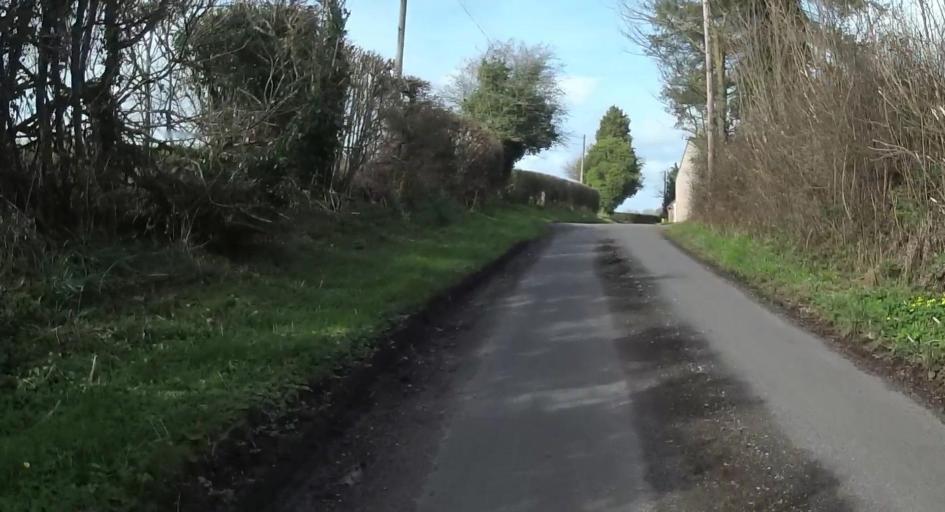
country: GB
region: England
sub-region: Hampshire
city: Kingsclere
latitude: 51.3467
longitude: -1.2408
